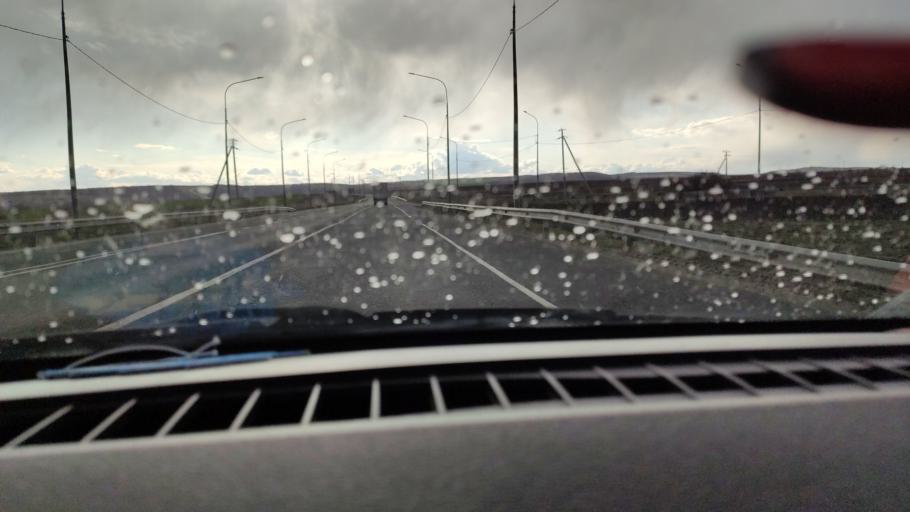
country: RU
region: Saratov
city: Yelshanka
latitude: 51.8300
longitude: 46.4115
